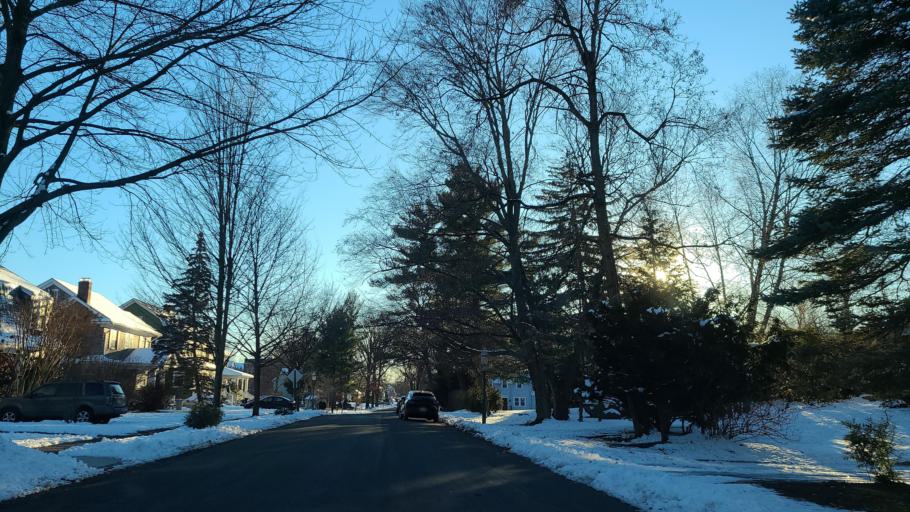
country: US
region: New Jersey
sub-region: Essex County
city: South Orange
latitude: 40.7559
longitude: -74.2551
